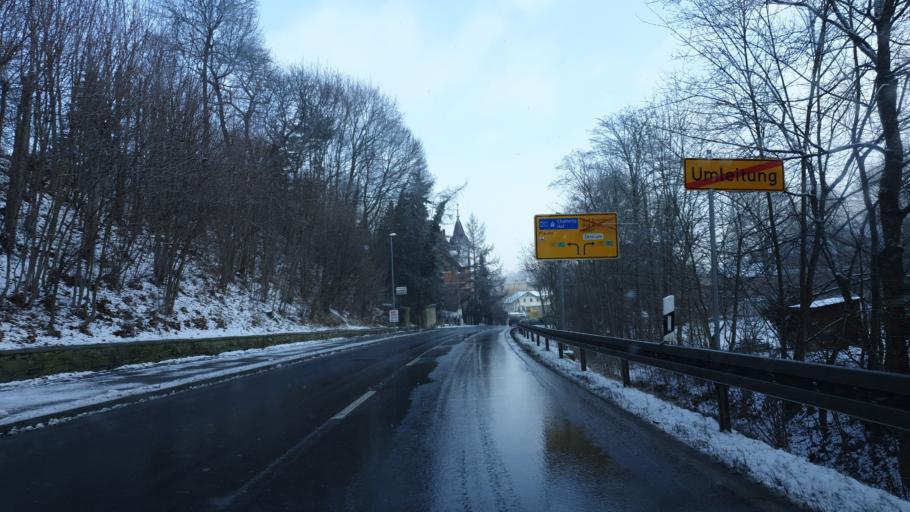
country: DE
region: Saxony
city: Oelsnitz
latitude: 50.4108
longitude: 12.1599
